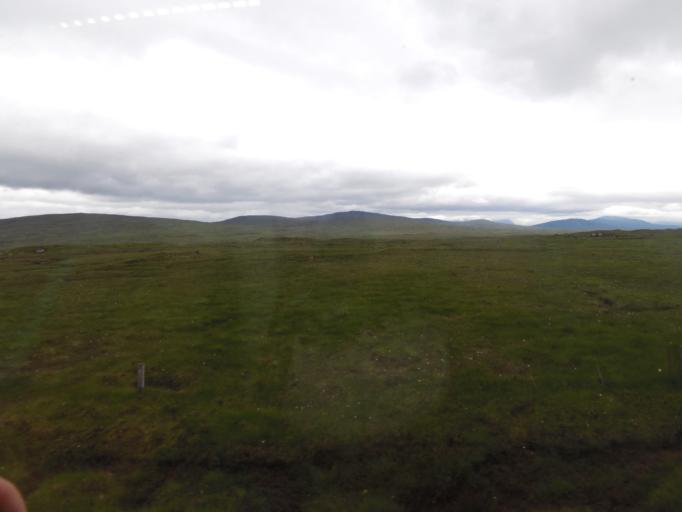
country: GB
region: Scotland
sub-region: Highland
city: Spean Bridge
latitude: 56.7214
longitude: -4.6245
